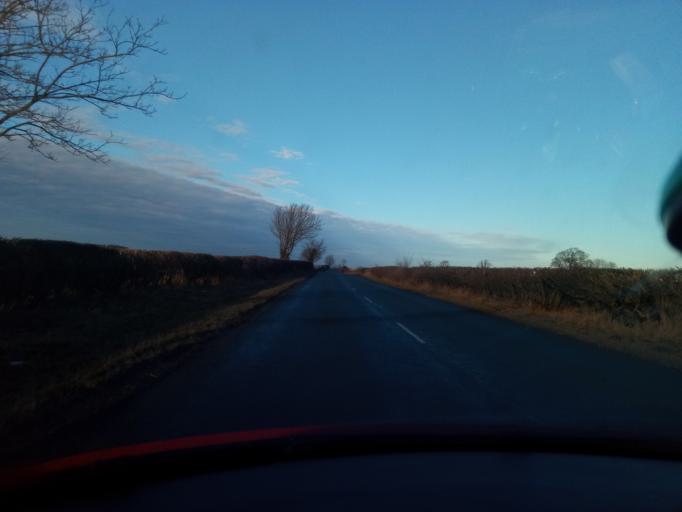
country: GB
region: England
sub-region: Darlington
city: High Coniscliffe
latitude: 54.4804
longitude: -1.6699
